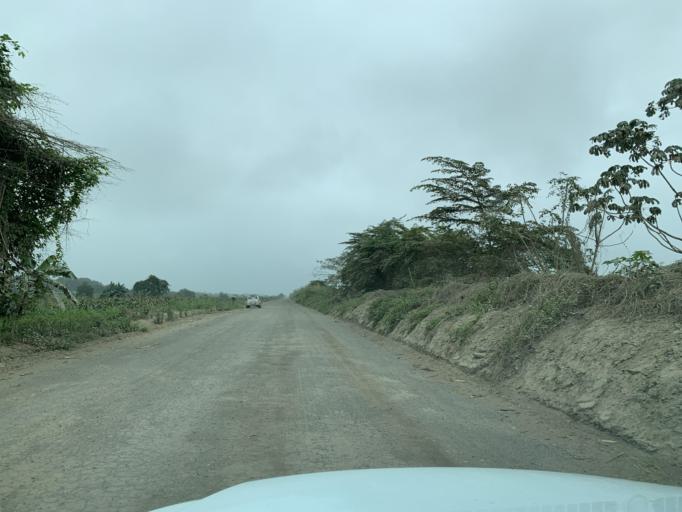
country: EC
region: Guayas
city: Coronel Marcelino Mariduena
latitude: -2.3597
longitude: -79.5524
